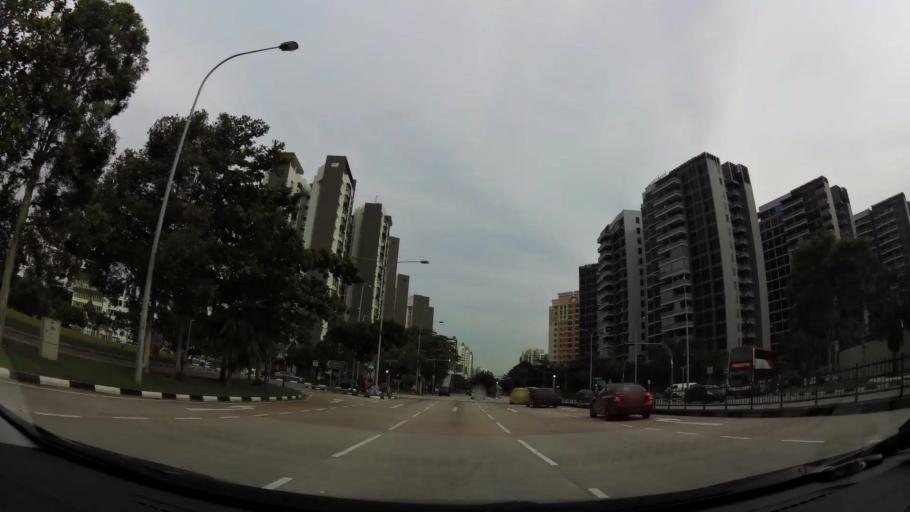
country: MY
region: Johor
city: Kampung Pasir Gudang Baru
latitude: 1.4047
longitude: 103.9035
